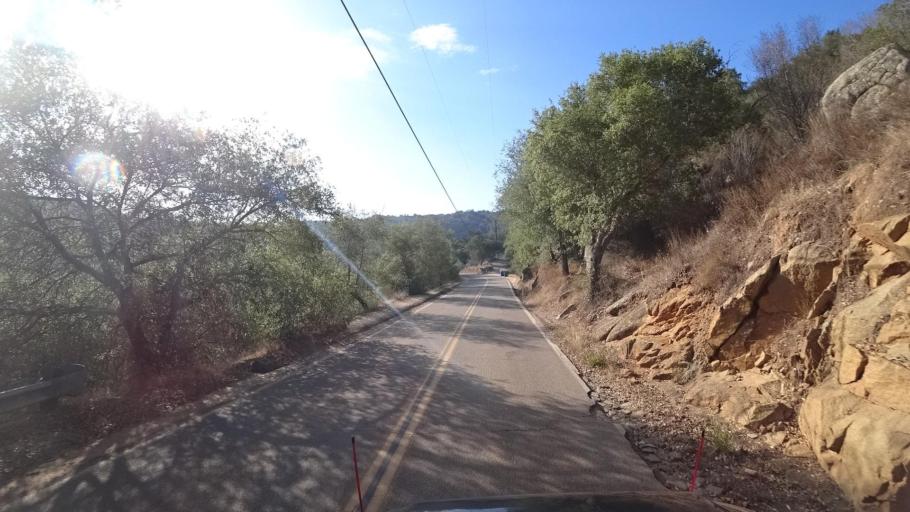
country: US
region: California
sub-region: San Diego County
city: Valley Center
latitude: 33.1677
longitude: -116.9989
